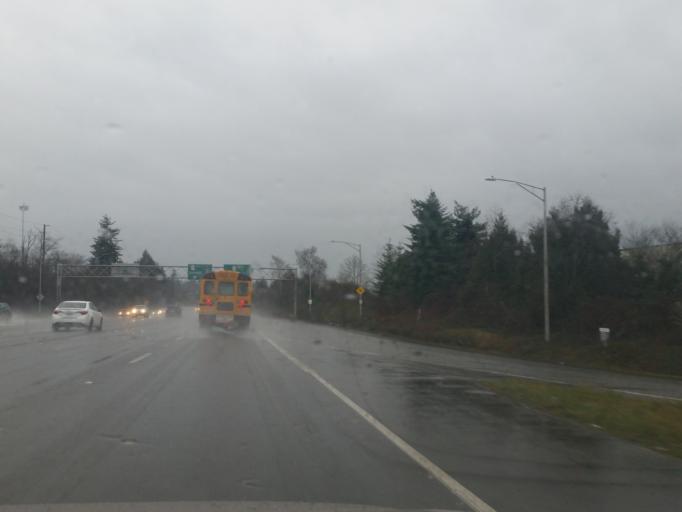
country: US
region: Washington
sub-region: Snohomish County
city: Mukilteo
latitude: 47.9288
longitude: -122.2608
